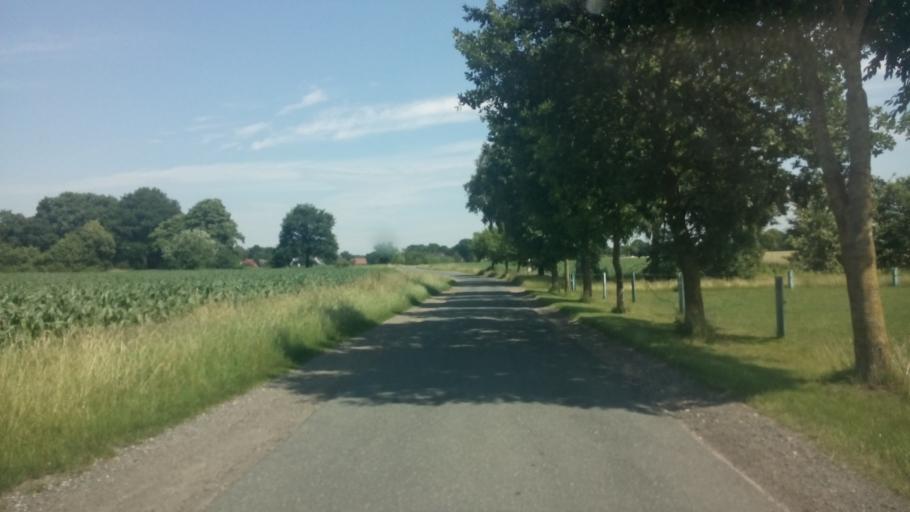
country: DE
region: Lower Saxony
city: Osterholz-Scharmbeck
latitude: 53.2563
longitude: 8.8190
